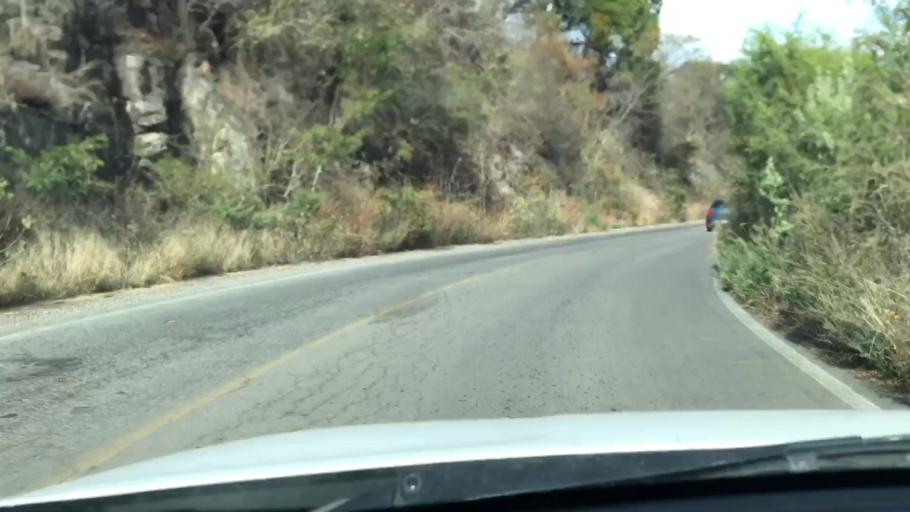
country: MX
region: Jalisco
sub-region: Zacoalco de Torres
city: Barranca de Otates (Barranca de Otatan)
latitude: 20.2405
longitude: -103.6842
